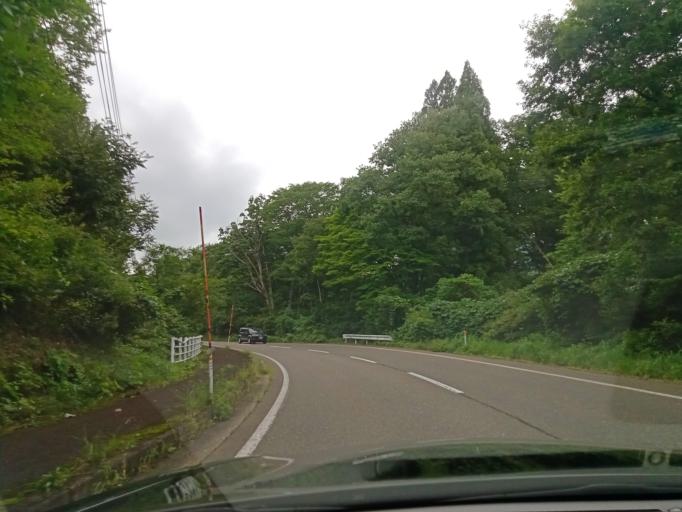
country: JP
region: Niigata
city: Arai
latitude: 36.8791
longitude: 138.1915
